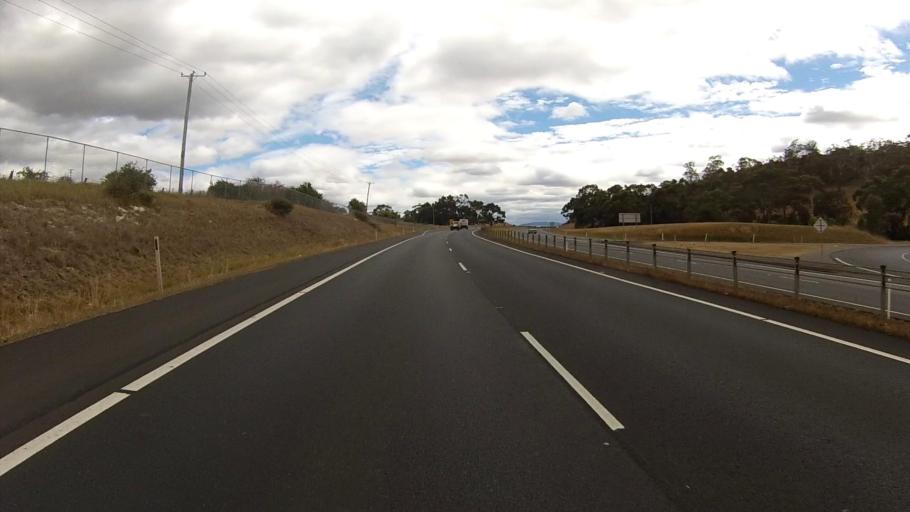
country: AU
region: Tasmania
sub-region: Glenorchy
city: Claremont
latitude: -42.7799
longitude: 147.2382
